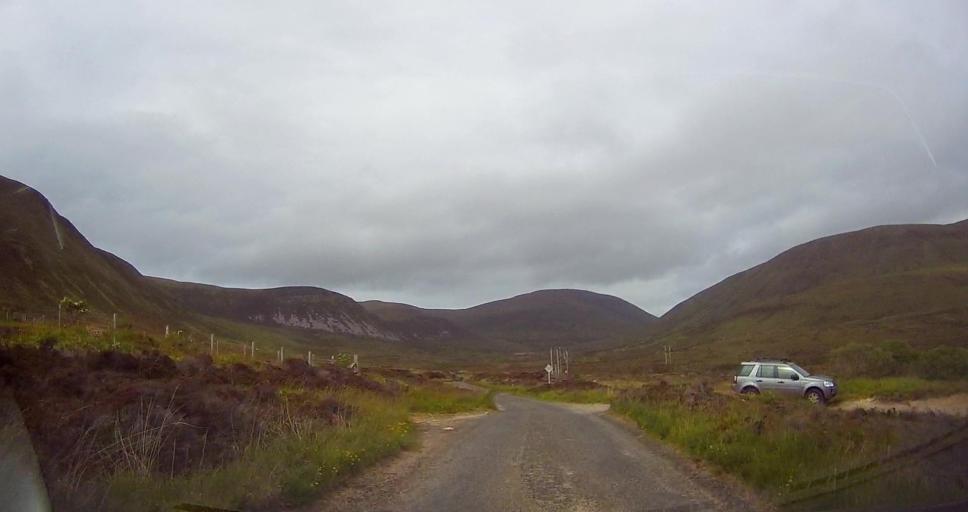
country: GB
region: Scotland
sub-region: Orkney Islands
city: Stromness
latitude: 58.8768
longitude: -3.3863
